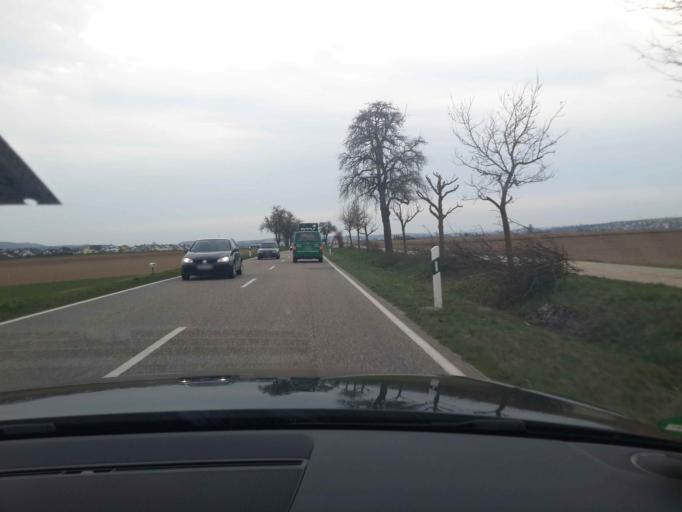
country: DE
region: Baden-Wuerttemberg
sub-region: Regierungsbezirk Stuttgart
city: Neuenstadt am Kocher
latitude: 49.2316
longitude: 9.3921
